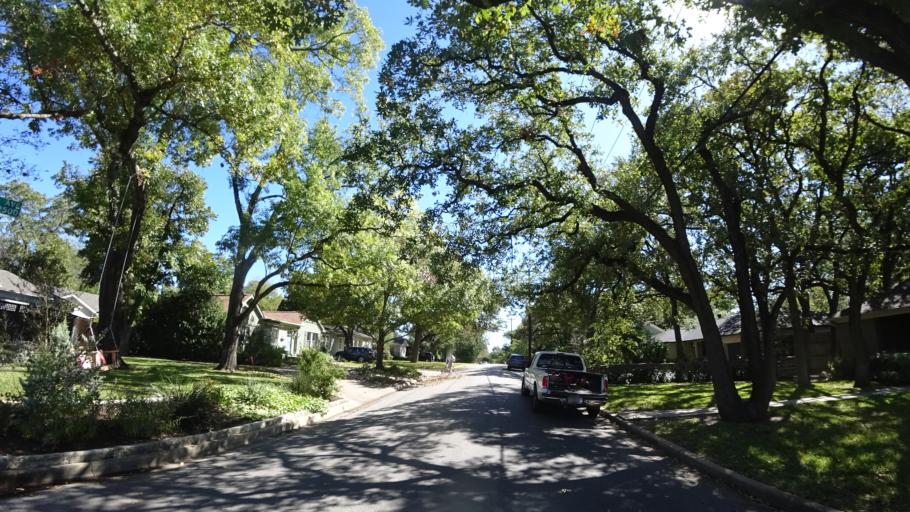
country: US
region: Texas
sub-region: Travis County
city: Rollingwood
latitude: 30.2975
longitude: -97.7665
